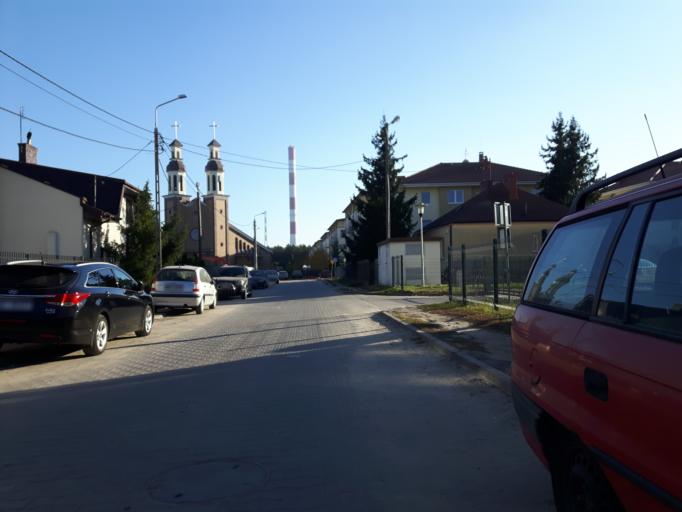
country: PL
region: Masovian Voivodeship
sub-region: Powiat wolominski
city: Zabki
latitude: 52.2801
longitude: 21.1254
